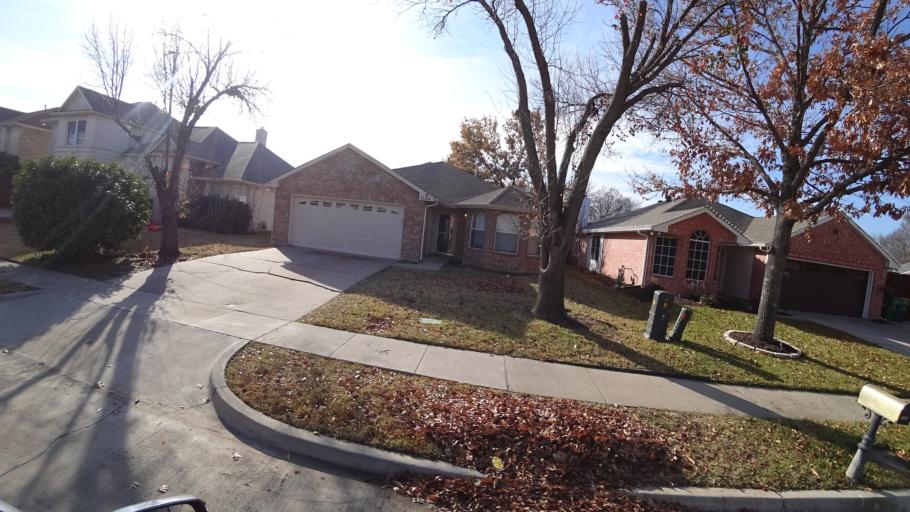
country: US
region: Texas
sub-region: Denton County
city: Lewisville
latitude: 33.0551
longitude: -97.0212
